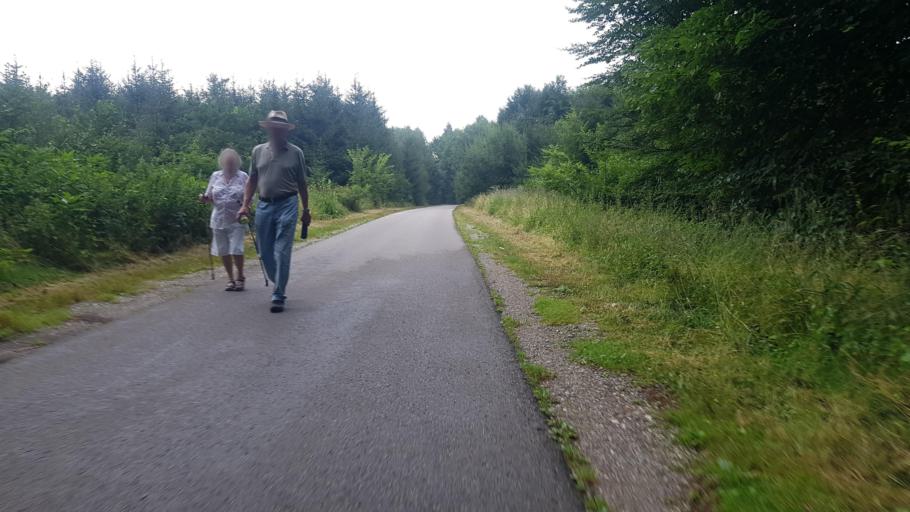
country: DE
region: Bavaria
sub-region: Upper Bavaria
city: Starnberg
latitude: 48.0195
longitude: 11.3473
